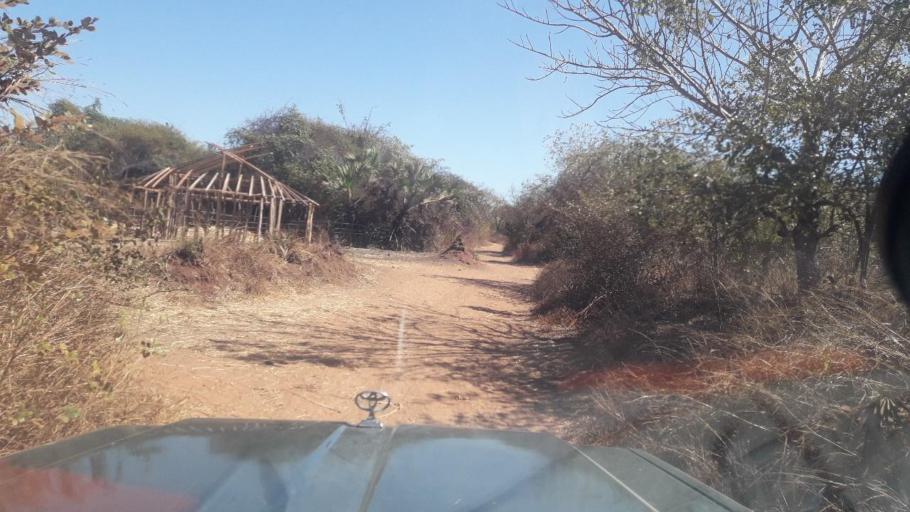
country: MG
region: Boeny
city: Sitampiky
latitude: -16.2490
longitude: 45.6812
